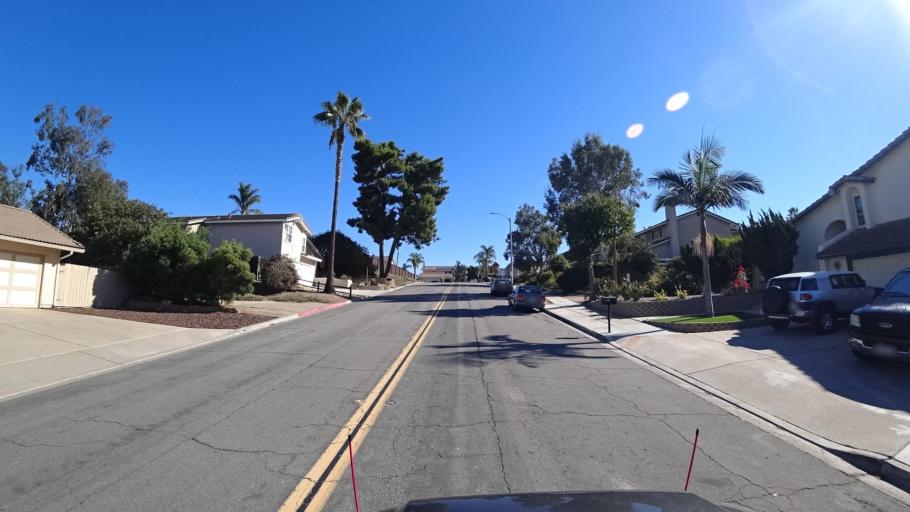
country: US
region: California
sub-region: San Diego County
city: Bonita
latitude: 32.6689
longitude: -117.0017
